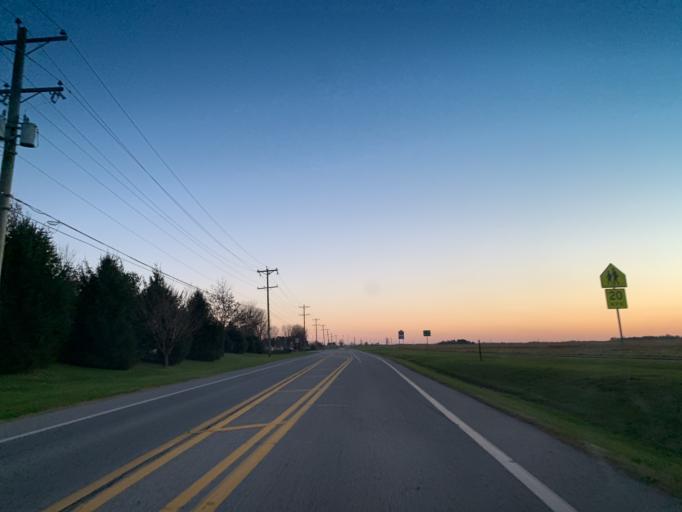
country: US
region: Delaware
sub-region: New Castle County
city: Middletown
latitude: 39.4253
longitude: -75.7404
